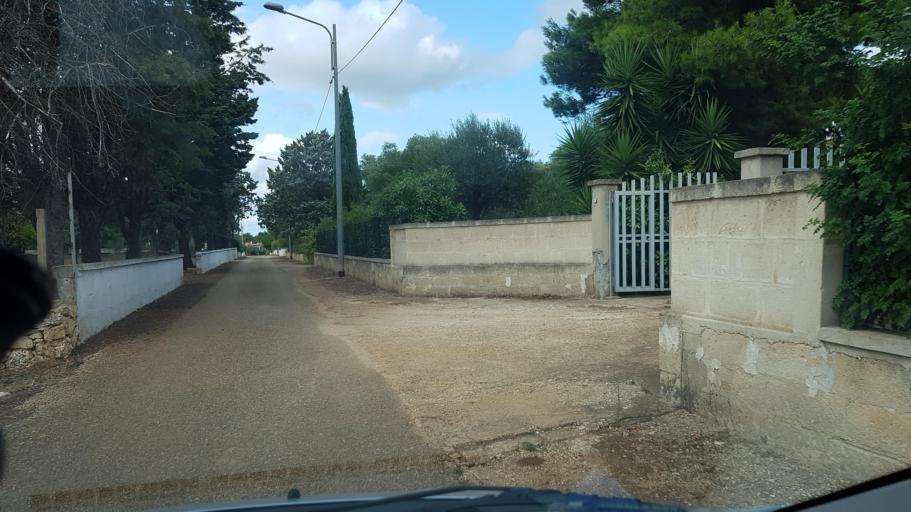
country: IT
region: Apulia
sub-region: Provincia di Brindisi
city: San Vito dei Normanni
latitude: 40.6654
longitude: 17.7219
